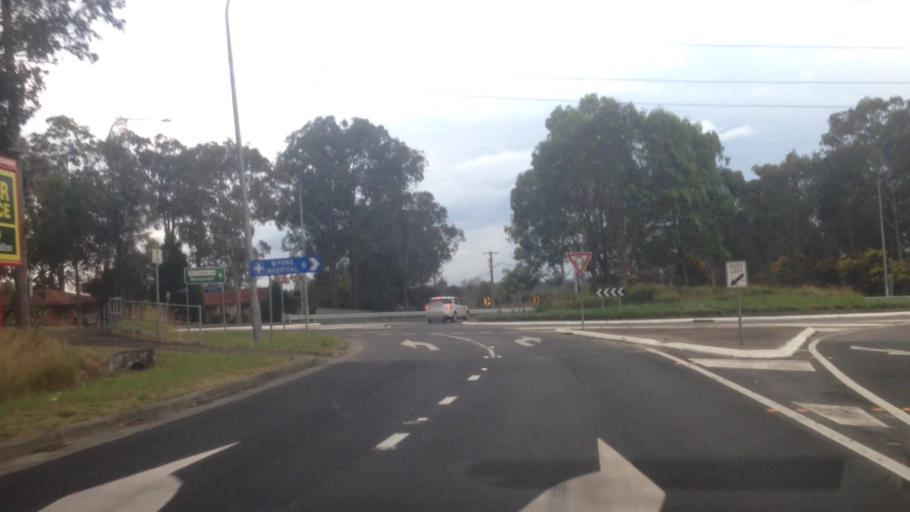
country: AU
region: New South Wales
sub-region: Wyong Shire
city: Jilliby
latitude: -33.2684
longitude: 151.4318
